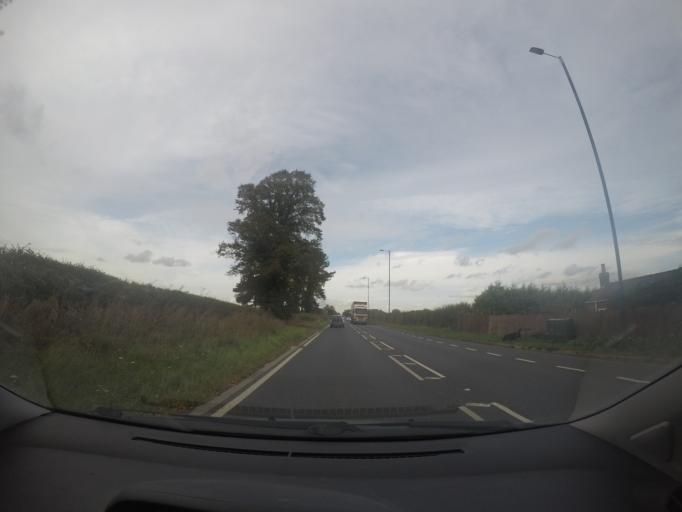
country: GB
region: England
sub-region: City of York
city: Deighton
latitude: 53.9147
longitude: -1.0534
